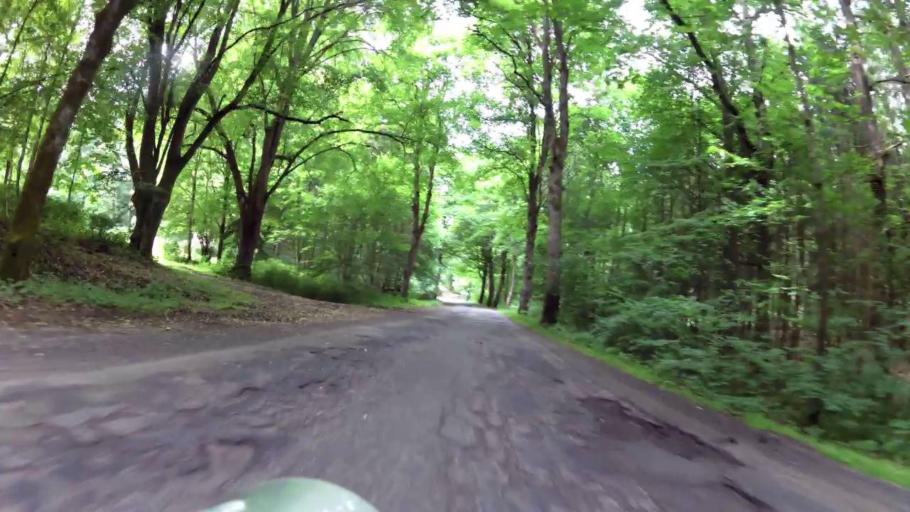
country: PL
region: West Pomeranian Voivodeship
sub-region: Powiat szczecinecki
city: Bialy Bor
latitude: 53.9646
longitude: 16.7282
